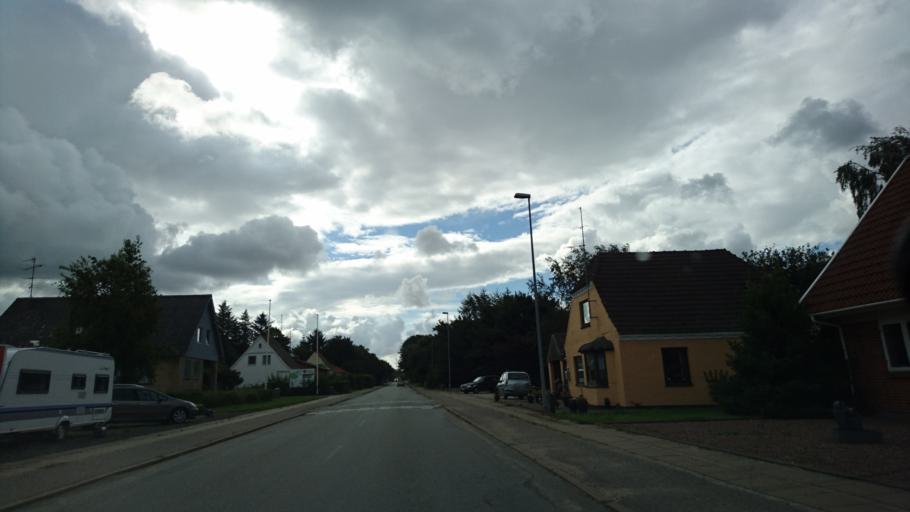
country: DK
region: North Denmark
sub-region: Hjorring Kommune
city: Tars
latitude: 57.3653
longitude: 10.1894
